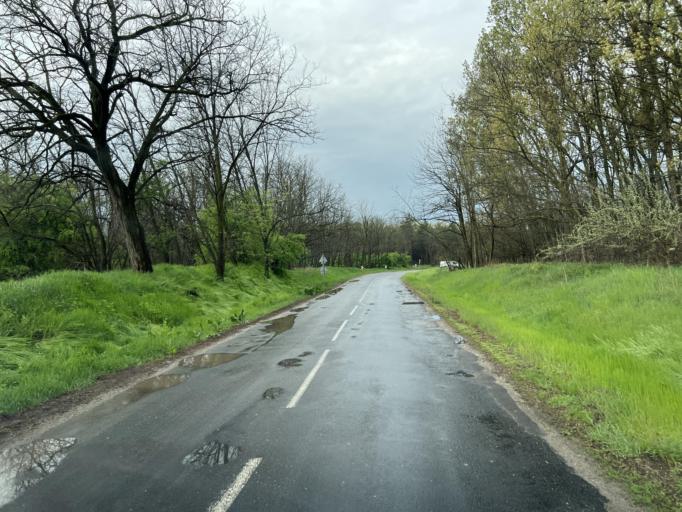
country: HU
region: Pest
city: Ujhartyan
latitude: 47.2282
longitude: 19.4278
